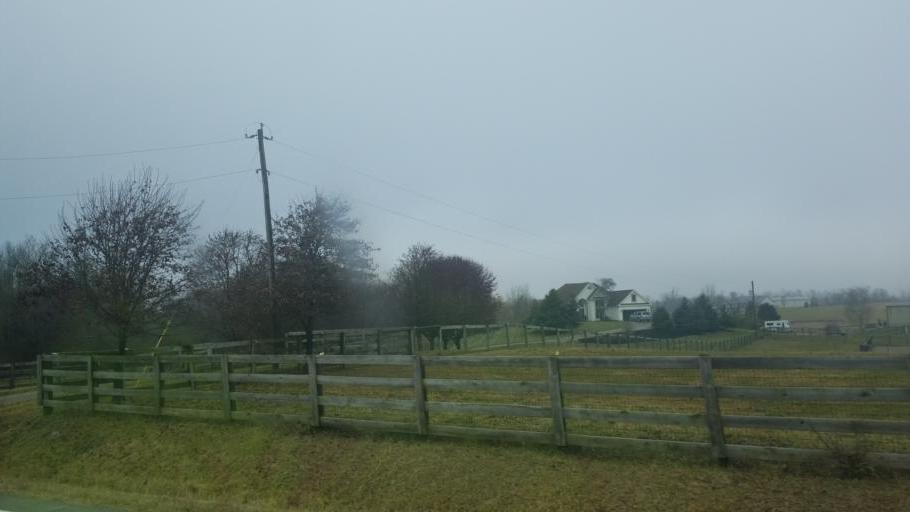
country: US
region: Ohio
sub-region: Champaign County
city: North Lewisburg
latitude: 40.2759
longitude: -83.5990
